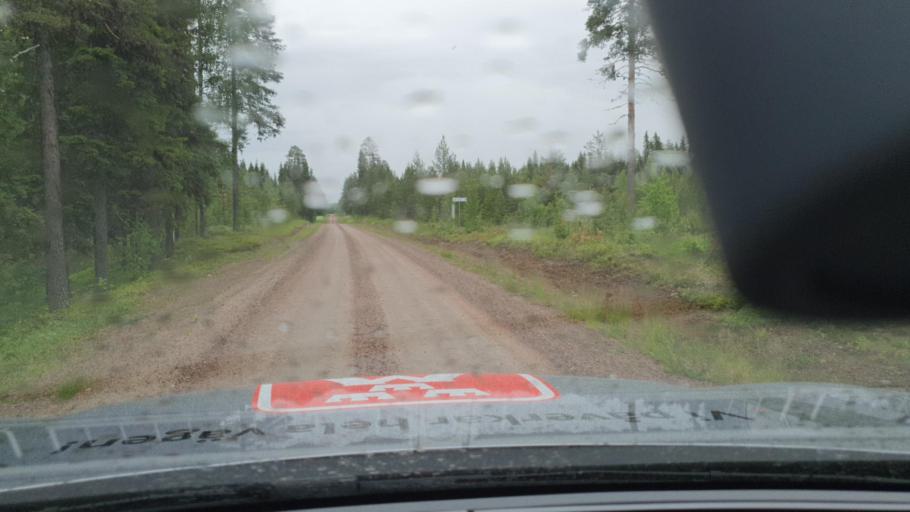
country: SE
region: Norrbotten
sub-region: Overkalix Kommun
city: OEverkalix
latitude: 66.5416
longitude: 22.7433
